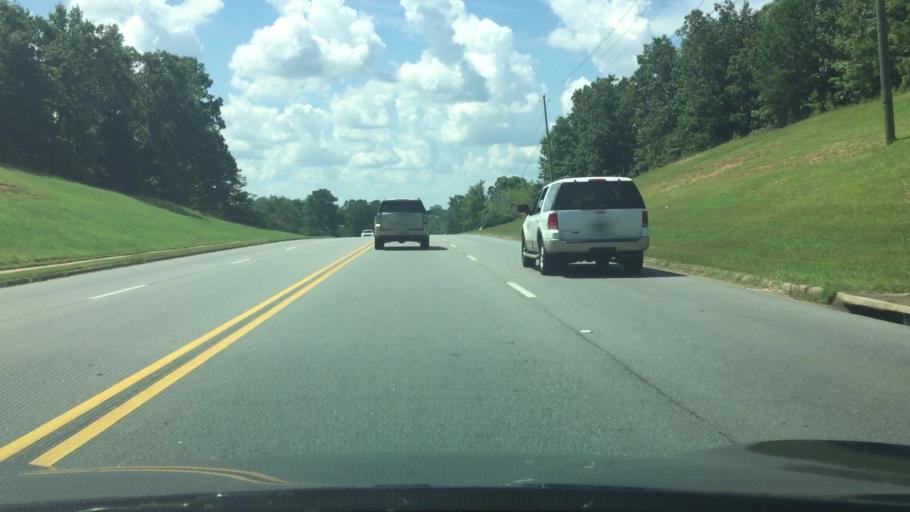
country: US
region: Alabama
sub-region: Lee County
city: Auburn
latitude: 32.6154
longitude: -85.4476
